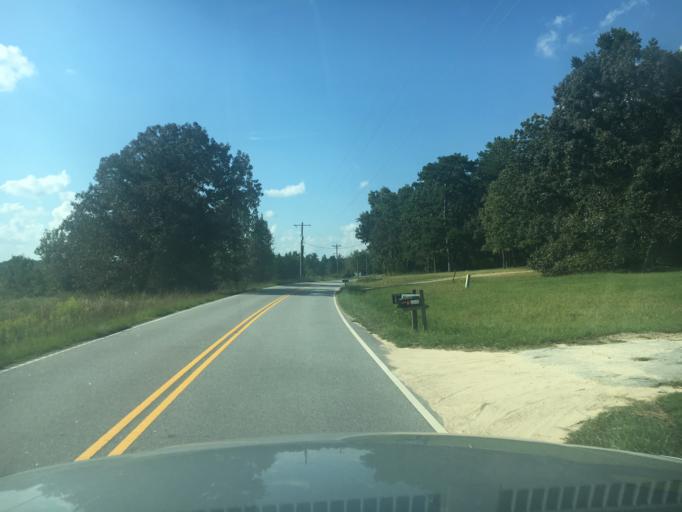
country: US
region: South Carolina
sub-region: Greenville County
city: Fountain Inn
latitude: 34.5579
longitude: -82.2143
